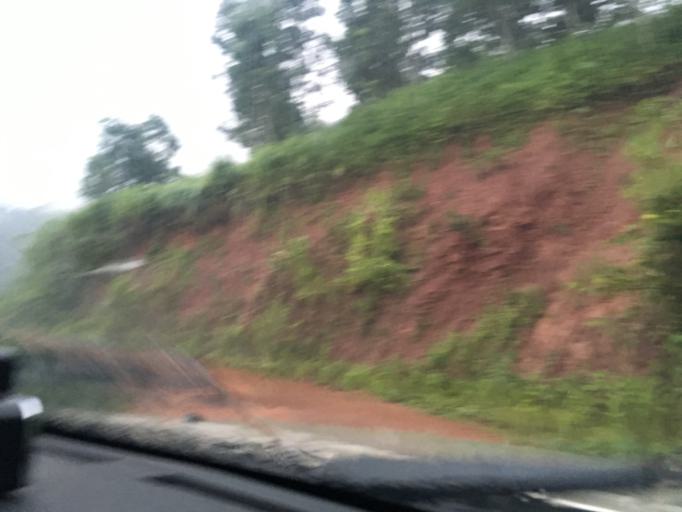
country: LA
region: Oudomxai
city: Muang La
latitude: 21.2412
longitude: 101.9480
